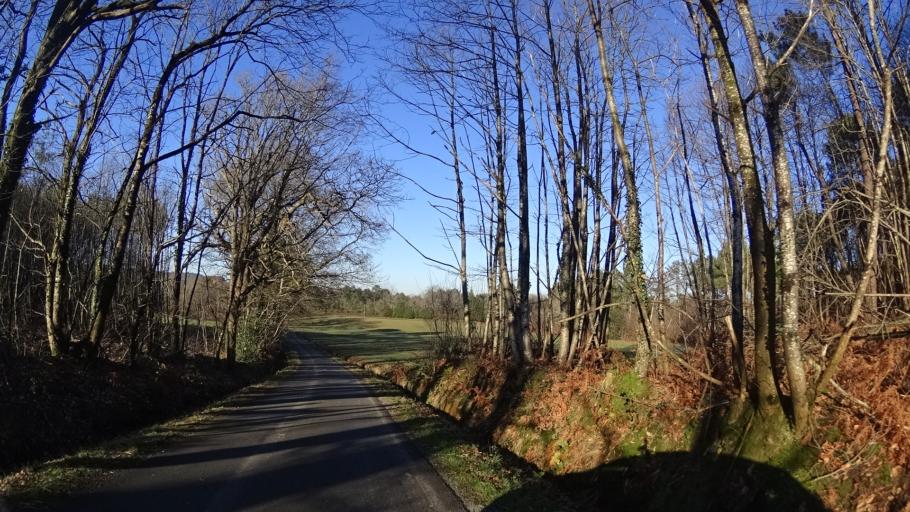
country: FR
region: Brittany
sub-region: Departement du Morbihan
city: Allaire
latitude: 47.6140
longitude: -2.1908
